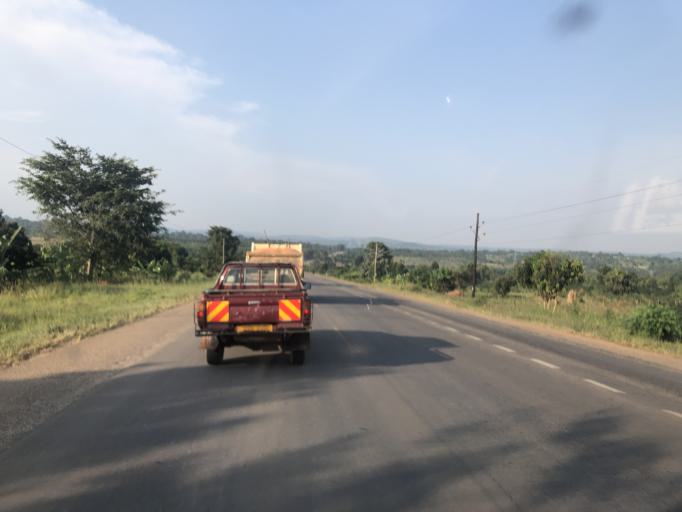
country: UG
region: Central Region
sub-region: Butambala District
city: Gombe
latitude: 0.0783
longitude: 32.1263
